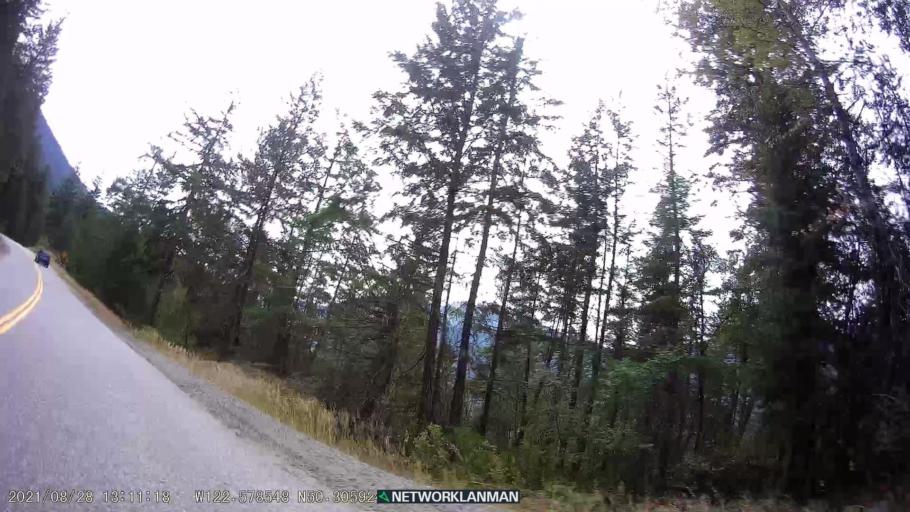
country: CA
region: British Columbia
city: Pemberton
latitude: 50.3053
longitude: -122.5796
